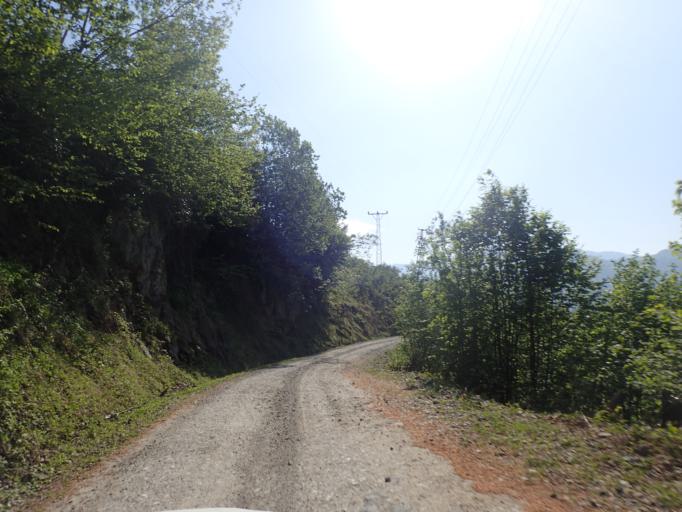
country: TR
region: Ordu
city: Topcam
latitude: 40.7068
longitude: 37.8635
